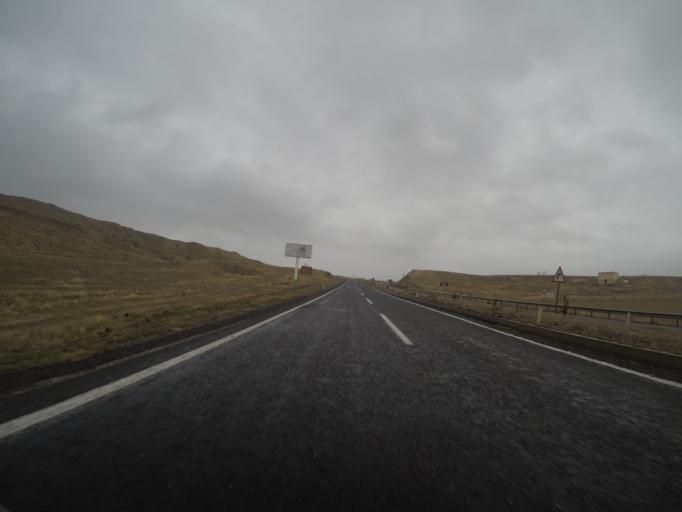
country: TR
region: Nevsehir
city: Avanos
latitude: 38.7055
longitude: 34.8724
